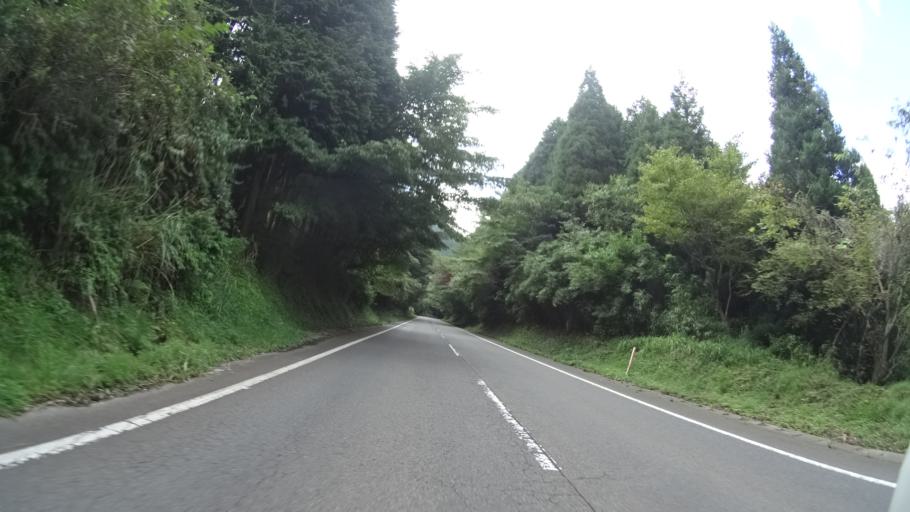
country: JP
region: Oita
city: Beppu
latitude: 33.3259
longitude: 131.4173
